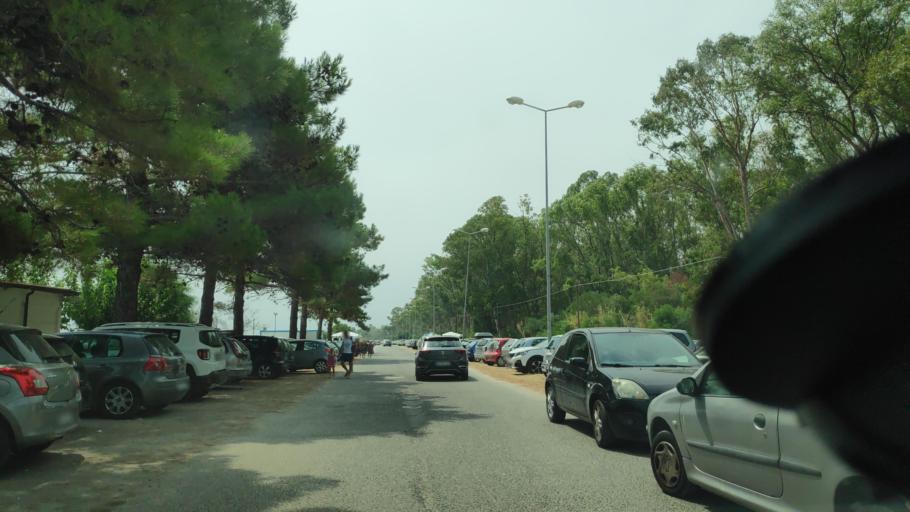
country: IT
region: Calabria
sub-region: Provincia di Catanzaro
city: Sant'Andrea Ionio Marina
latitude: 38.6167
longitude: 16.5605
